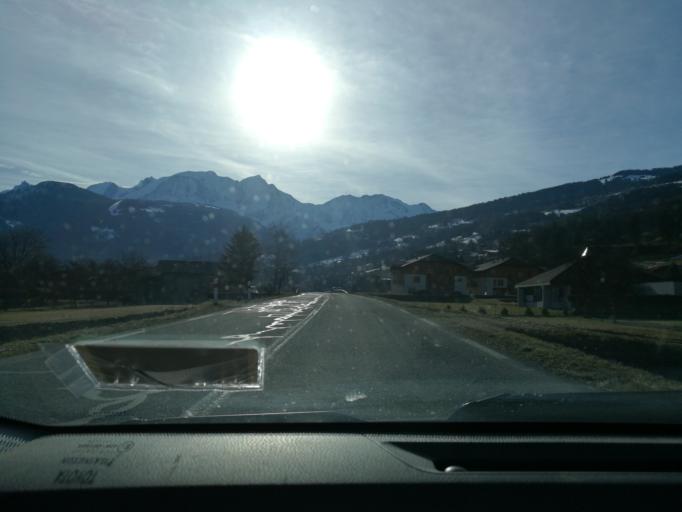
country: FR
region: Rhone-Alpes
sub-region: Departement de la Haute-Savoie
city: Domancy
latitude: 45.9125
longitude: 6.6534
